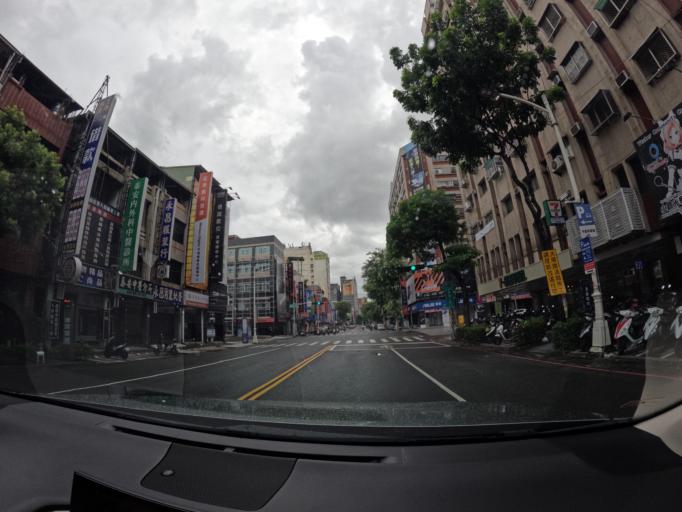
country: TW
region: Kaohsiung
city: Kaohsiung
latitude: 22.6375
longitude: 120.3082
